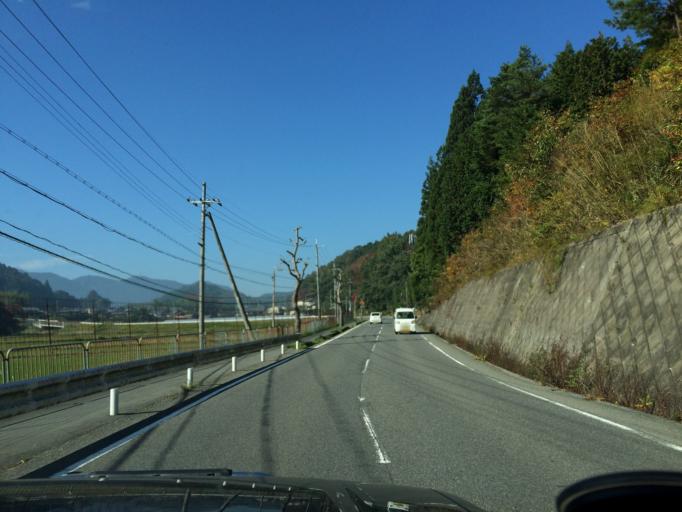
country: JP
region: Kyoto
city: Kameoka
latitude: 35.0534
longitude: 135.5137
